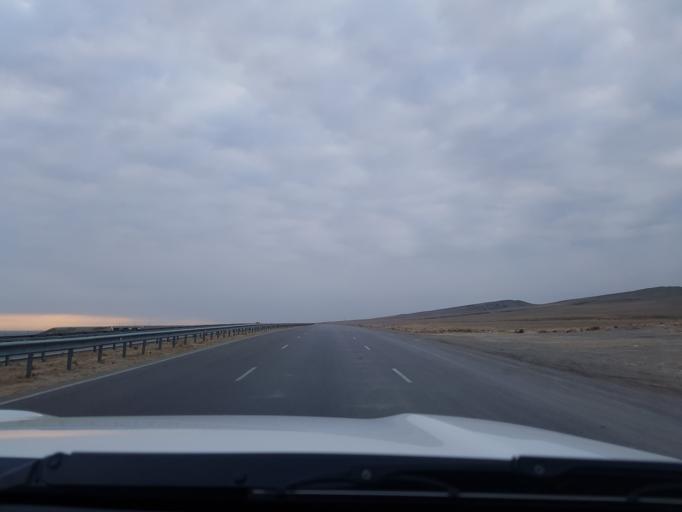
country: IR
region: Razavi Khorasan
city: Dargaz
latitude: 37.6845
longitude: 59.0696
